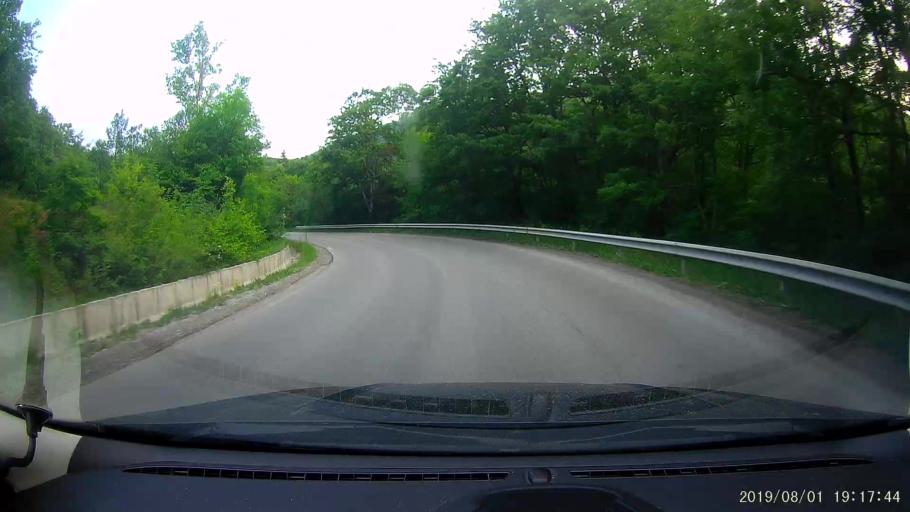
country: BG
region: Shumen
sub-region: Obshtina Smyadovo
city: Smyadovo
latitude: 42.9200
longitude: 26.9396
